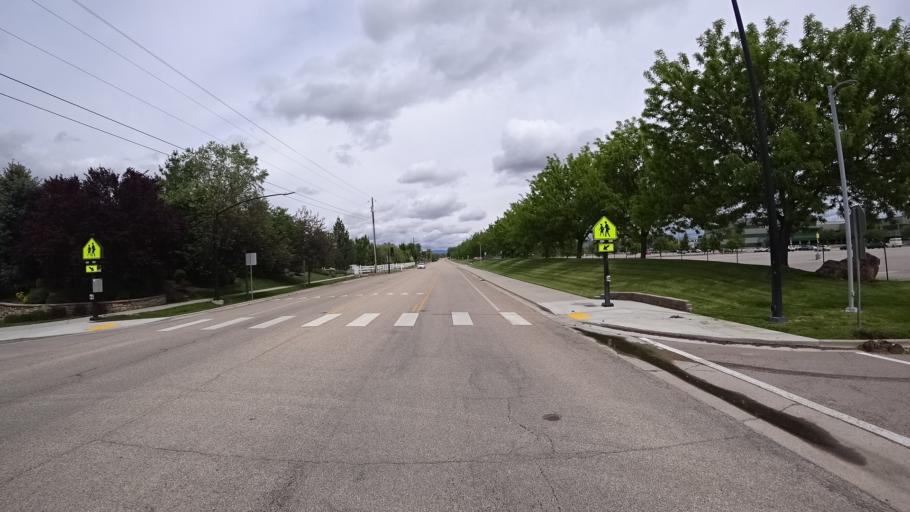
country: US
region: Idaho
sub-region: Ada County
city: Eagle
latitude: 43.6997
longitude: -116.4036
